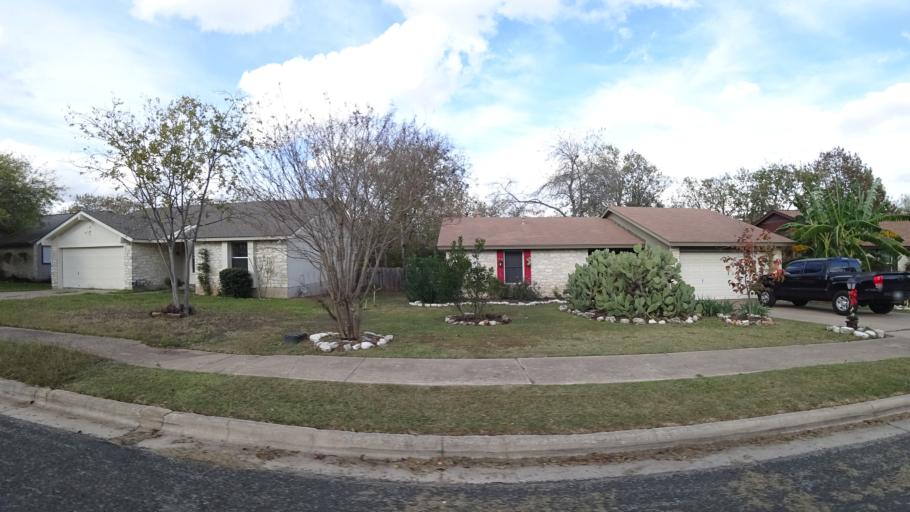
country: US
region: Texas
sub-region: Williamson County
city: Brushy Creek
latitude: 30.5123
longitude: -97.7345
